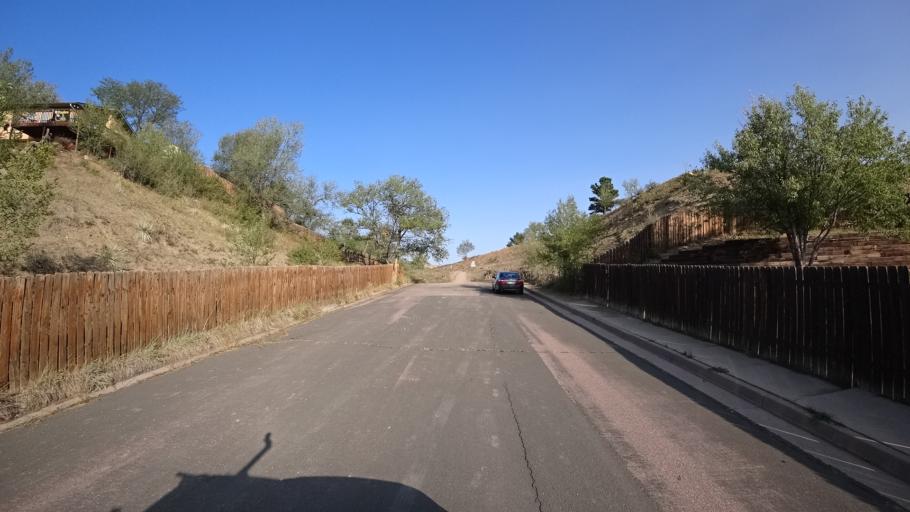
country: US
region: Colorado
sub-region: El Paso County
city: Colorado Springs
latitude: 38.8170
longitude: -104.8515
